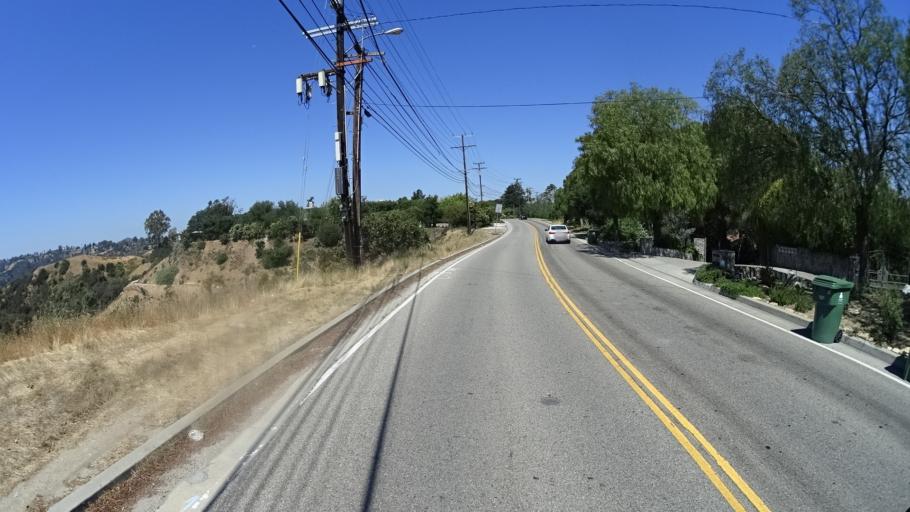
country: US
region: California
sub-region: Los Angeles County
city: Sherman Oaks
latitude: 34.1318
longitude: -118.4513
